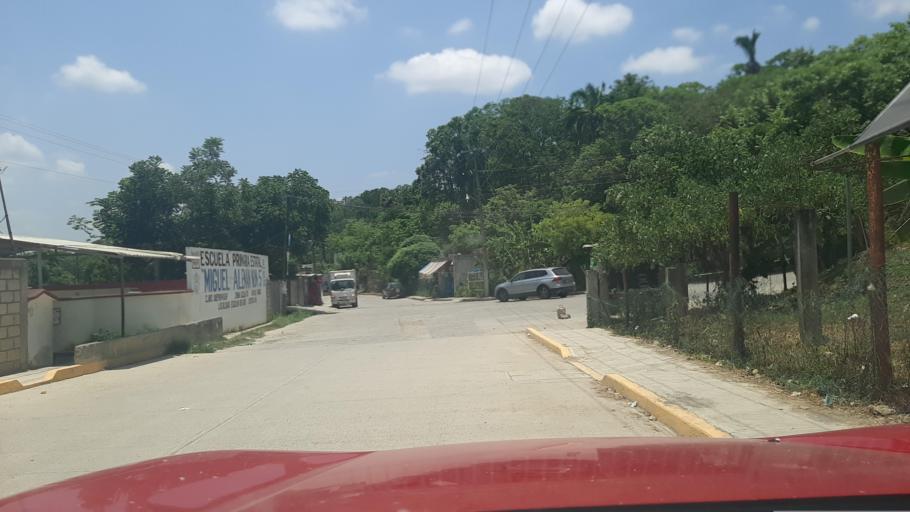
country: MX
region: Veracruz
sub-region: Poza Rica de Hidalgo
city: Arroyo del Maiz Uno
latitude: 20.4984
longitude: -97.4244
